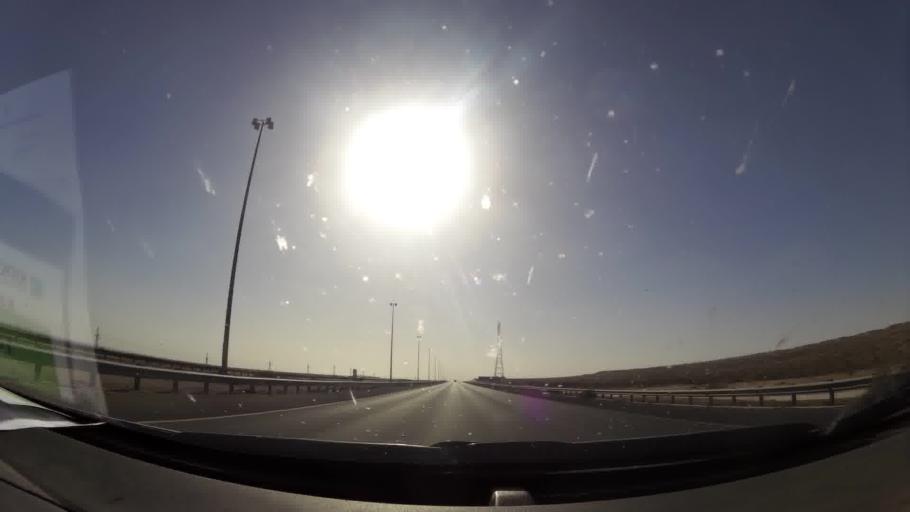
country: KW
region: Al Asimah
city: Kuwait City
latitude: 29.5580
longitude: 47.8830
